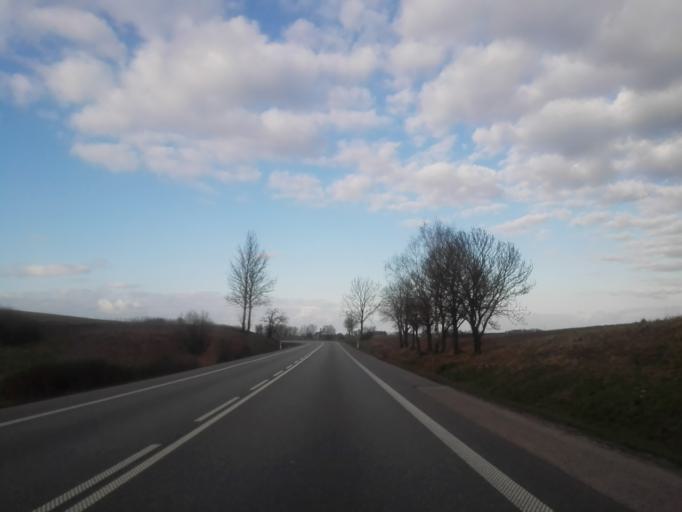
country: PL
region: Podlasie
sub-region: Suwalki
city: Suwalki
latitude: 54.1894
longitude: 23.0082
